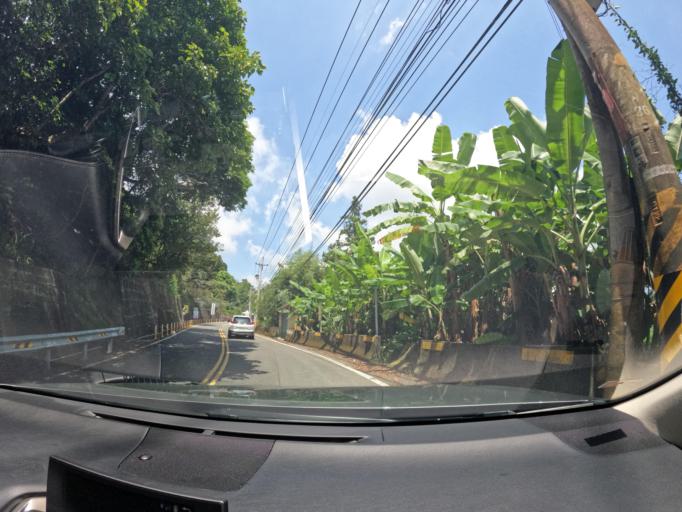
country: TW
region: Taiwan
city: Fengyuan
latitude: 24.3854
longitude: 120.8227
